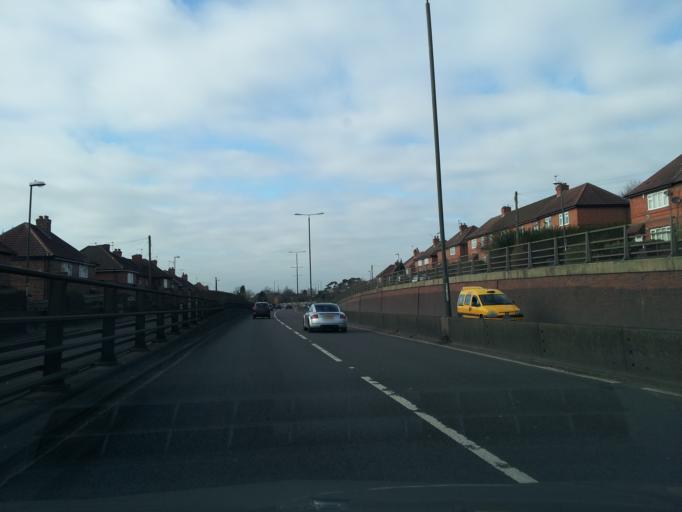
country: GB
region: England
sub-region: Derbyshire
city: Borrowash
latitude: 52.9162
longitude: -1.4018
